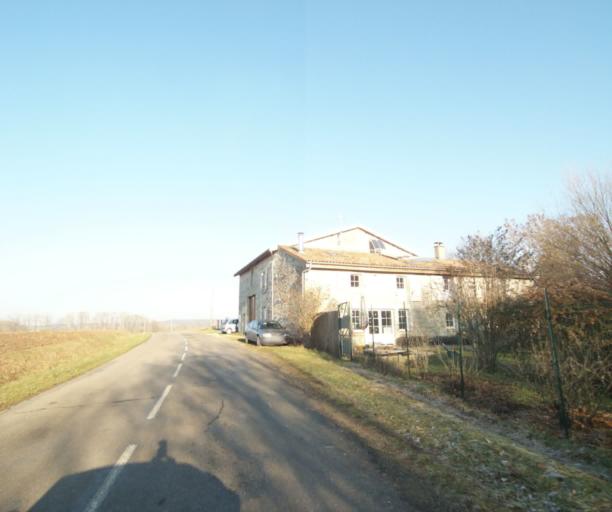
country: FR
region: Champagne-Ardenne
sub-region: Departement de la Haute-Marne
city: Bienville
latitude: 48.5982
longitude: 5.0811
